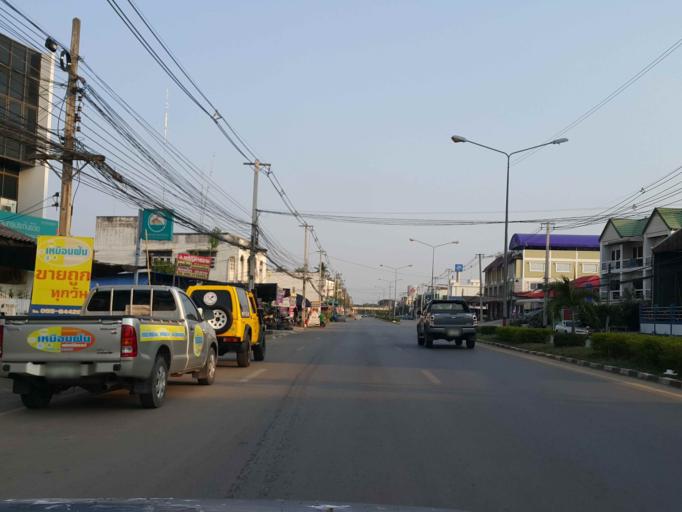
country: TH
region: Sukhothai
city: Sawankhalok
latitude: 17.3000
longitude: 99.8351
